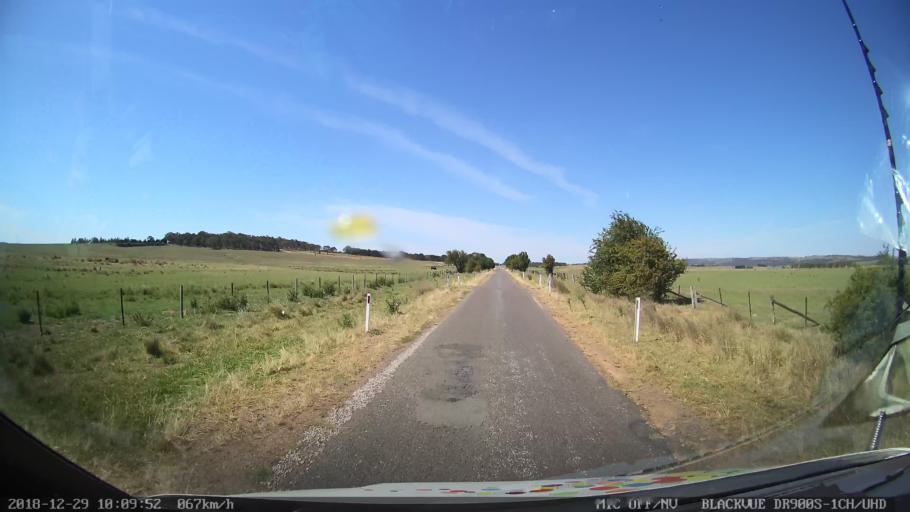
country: AU
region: New South Wales
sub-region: Yass Valley
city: Gundaroo
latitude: -34.8701
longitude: 149.4590
